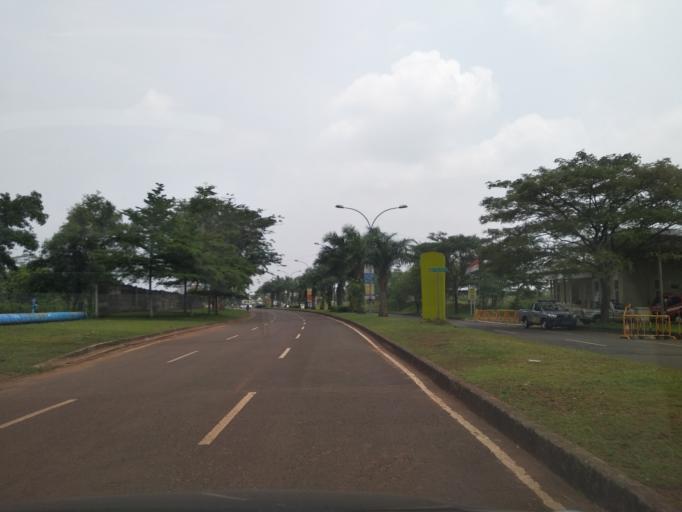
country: ID
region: West Java
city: Bekasi
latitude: -6.2943
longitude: 107.0478
